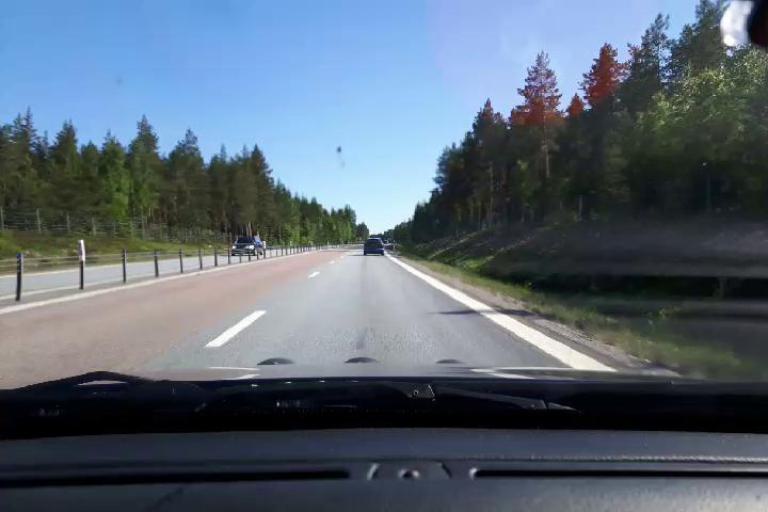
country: SE
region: Gaevleborg
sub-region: Gavle Kommun
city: Norrsundet
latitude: 60.8822
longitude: 17.0449
